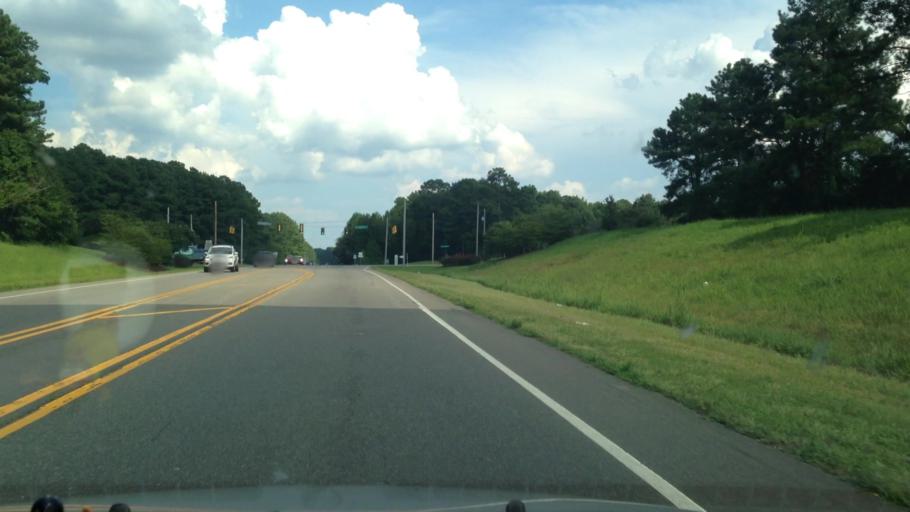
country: US
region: North Carolina
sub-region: Lee County
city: Broadway
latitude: 35.4449
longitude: -79.1117
